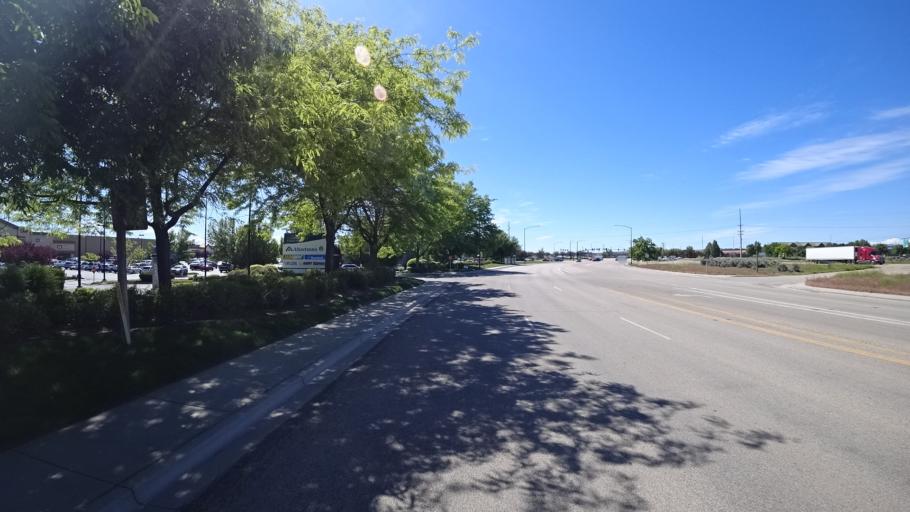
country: US
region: Idaho
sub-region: Ada County
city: Boise
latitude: 43.5429
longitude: -116.1558
